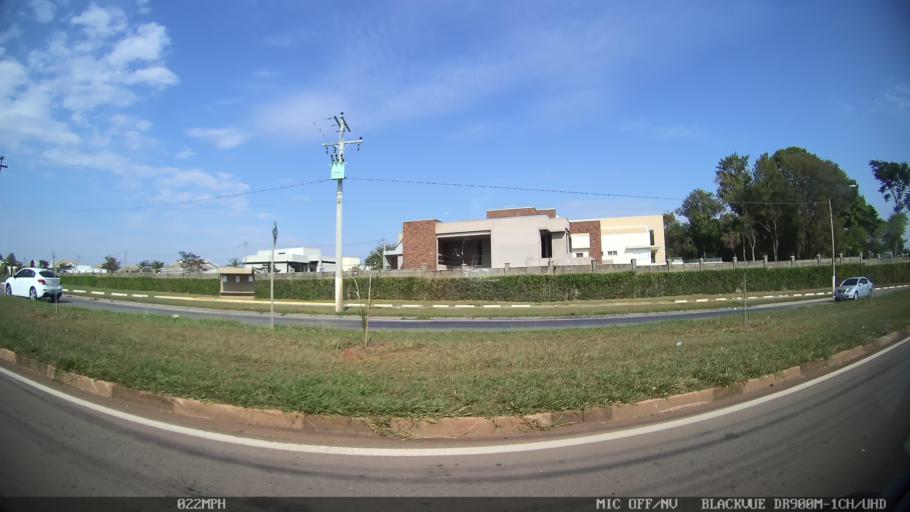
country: BR
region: Sao Paulo
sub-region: Paulinia
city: Paulinia
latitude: -22.7591
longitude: -47.1403
